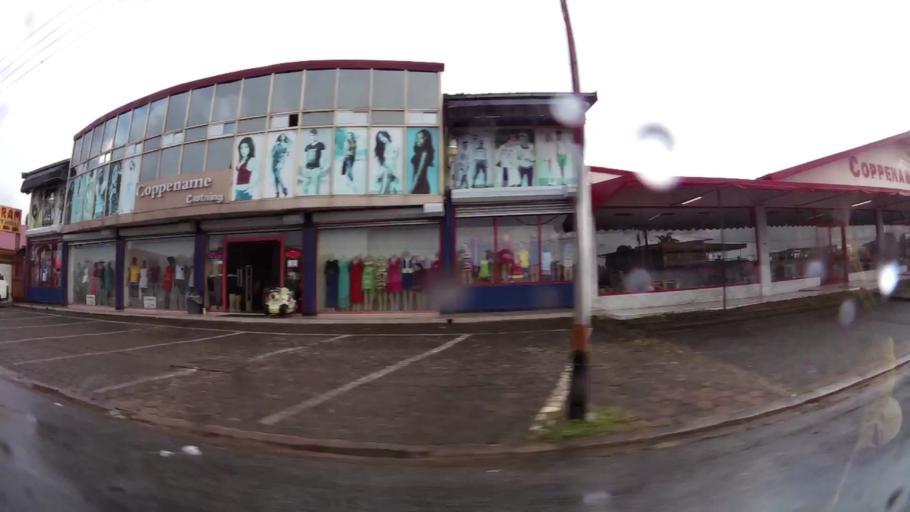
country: SR
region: Paramaribo
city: Paramaribo
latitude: 5.8148
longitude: -55.1880
